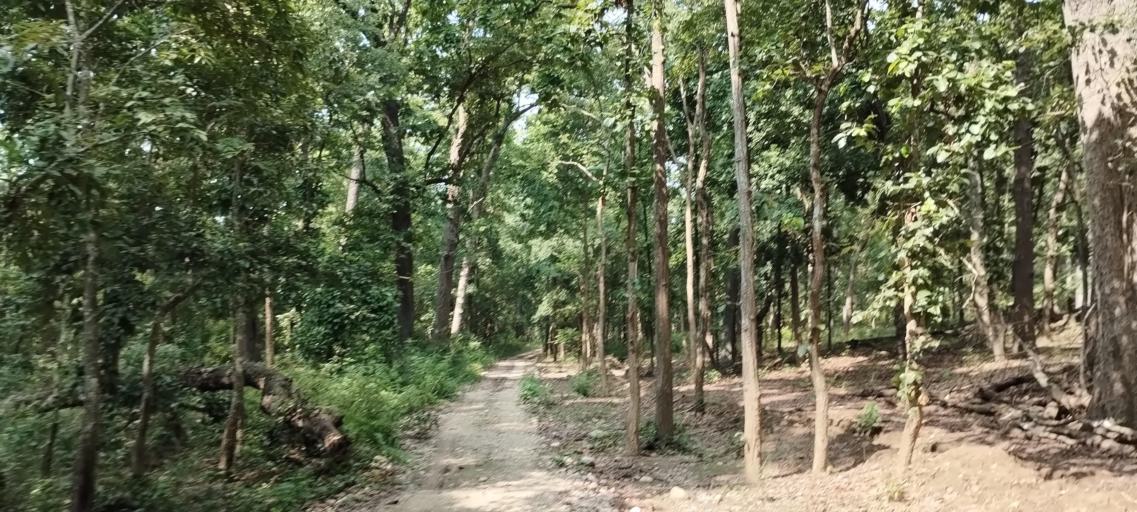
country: NP
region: Far Western
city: Tikapur
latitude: 28.5187
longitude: 81.2542
